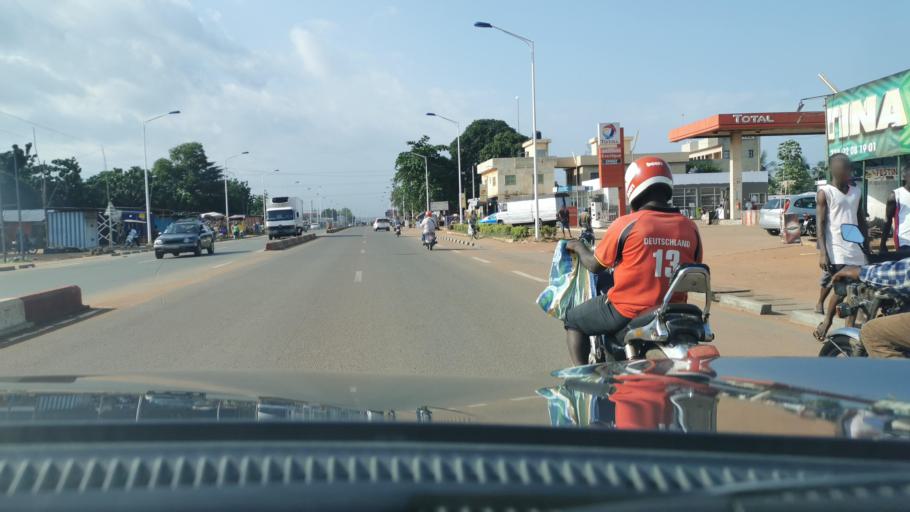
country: TG
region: Maritime
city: Lome
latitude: 6.2041
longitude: 1.2419
